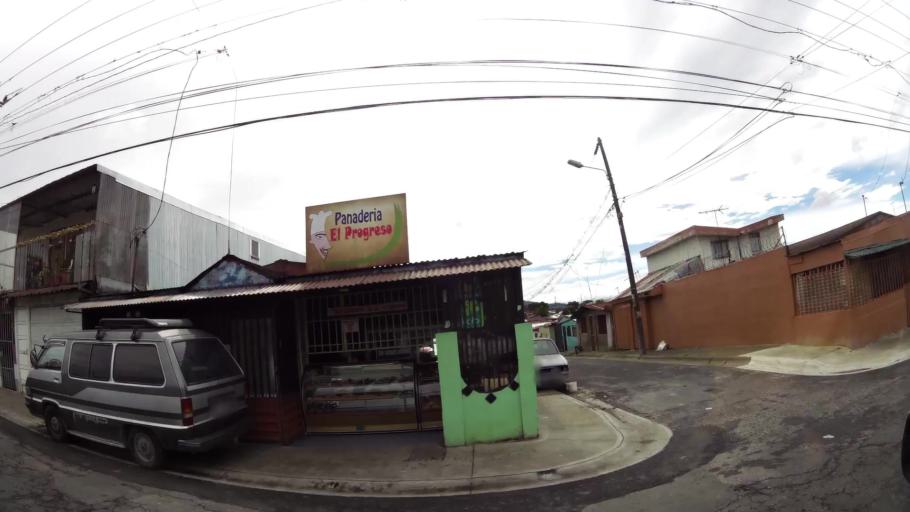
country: CR
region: San Jose
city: Ipis
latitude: 9.9613
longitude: -84.0121
